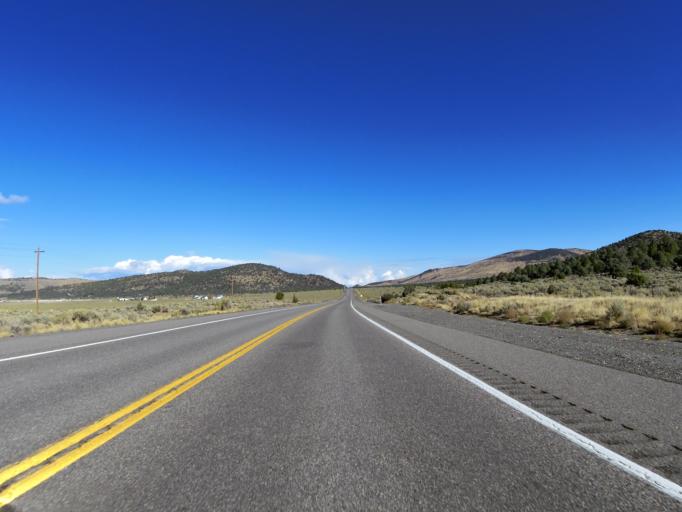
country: US
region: Nevada
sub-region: Douglas County
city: Gardnerville Ranchos
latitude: 38.7904
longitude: -119.5972
